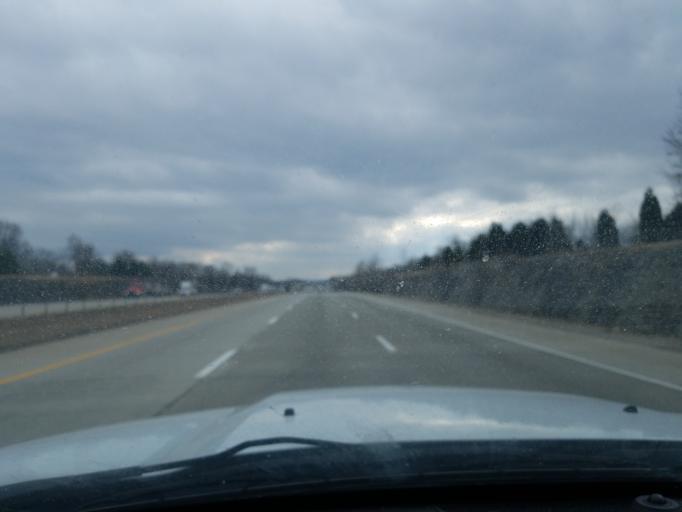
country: US
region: Kentucky
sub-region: Bullitt County
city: Brooks
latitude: 38.0320
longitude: -85.6968
